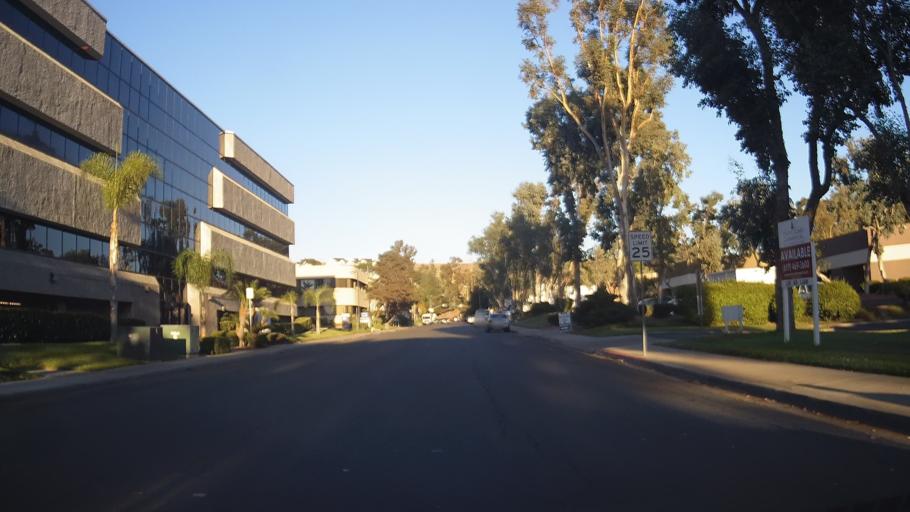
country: US
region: California
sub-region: San Diego County
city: Poway
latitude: 32.9138
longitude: -117.1136
